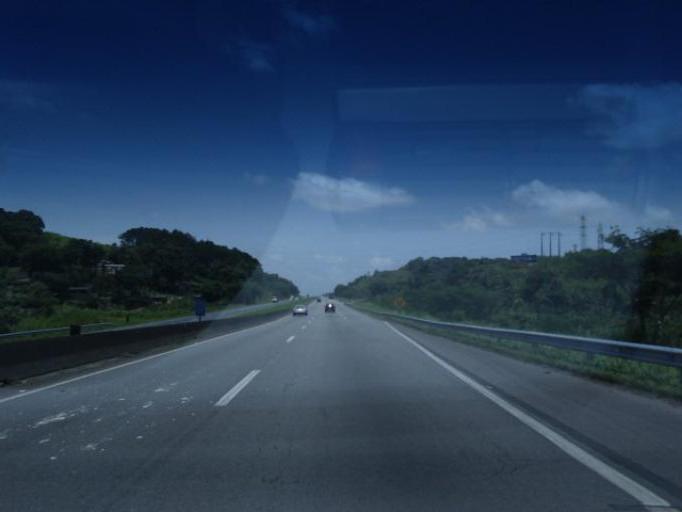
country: BR
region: Sao Paulo
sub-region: Juquia
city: Juquia
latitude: -24.3334
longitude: -47.6012
